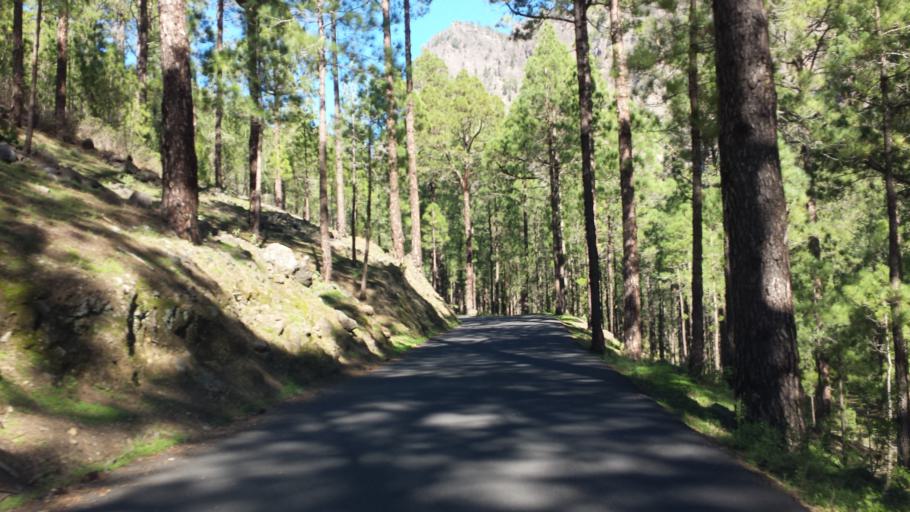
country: ES
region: Canary Islands
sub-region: Provincia de Santa Cruz de Tenerife
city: El Paso
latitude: 28.6833
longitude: -17.8481
